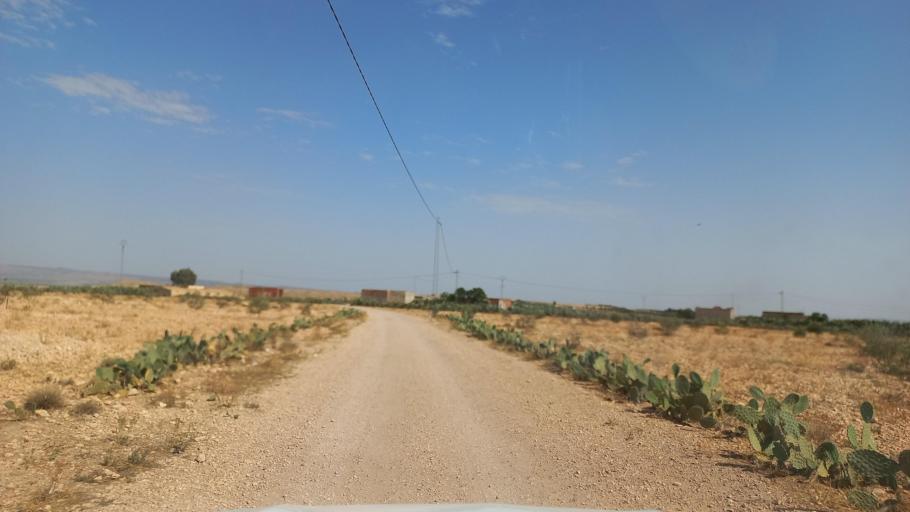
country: TN
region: Al Qasrayn
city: Kasserine
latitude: 35.2797
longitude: 8.9578
